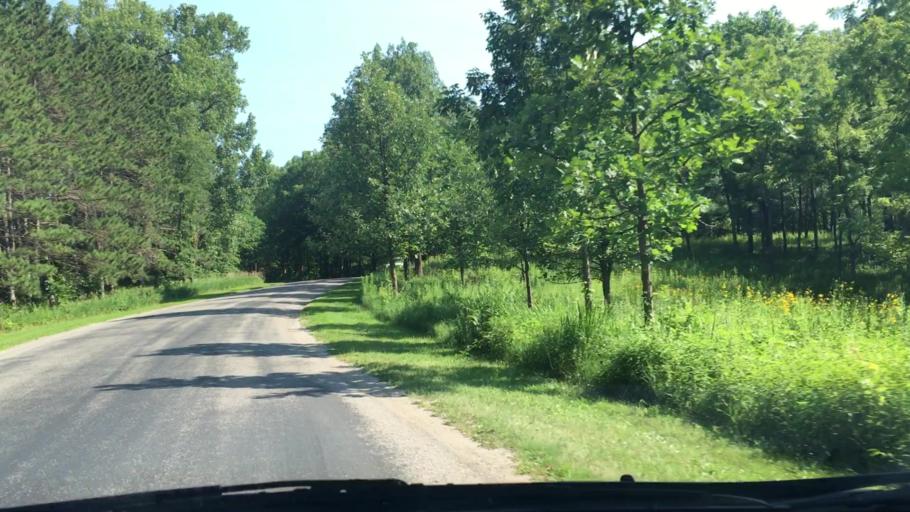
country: US
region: Iowa
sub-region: Johnson County
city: Tiffin
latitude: 41.7283
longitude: -91.7244
